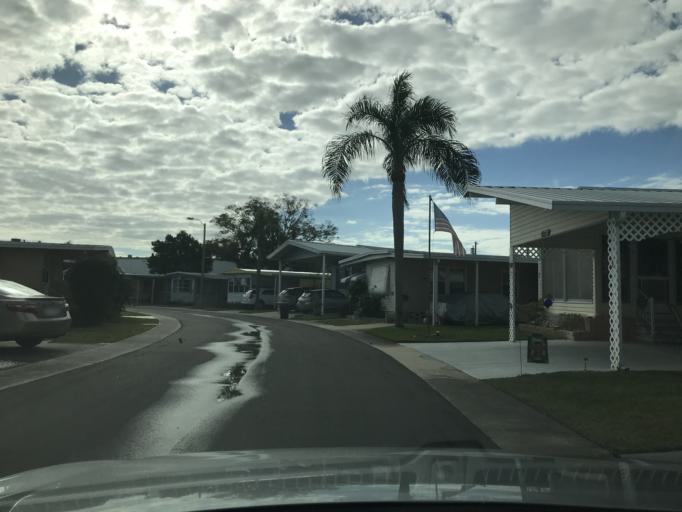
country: US
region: Florida
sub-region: Pinellas County
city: Largo
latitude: 27.9239
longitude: -82.7907
